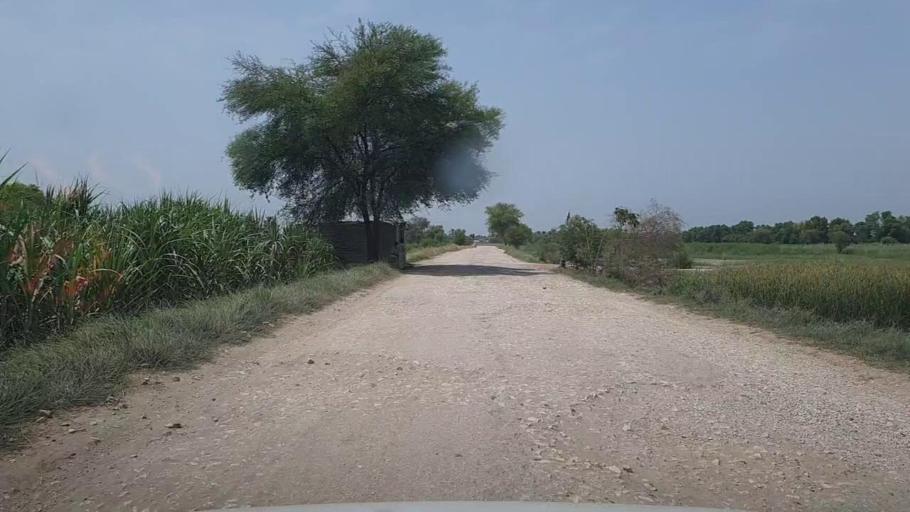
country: PK
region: Sindh
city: Pano Aqil
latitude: 27.8496
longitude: 69.1429
